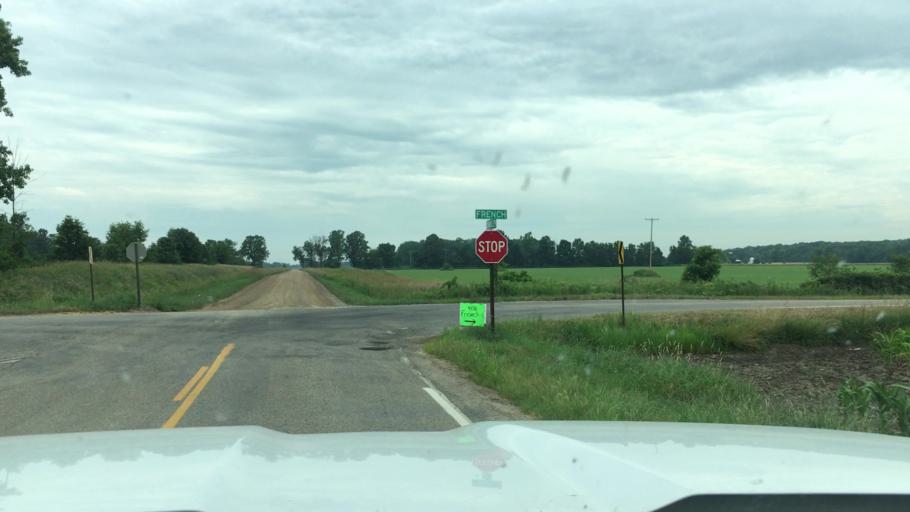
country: US
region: Michigan
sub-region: Clinton County
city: Saint Johns
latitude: 43.0597
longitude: -84.4840
